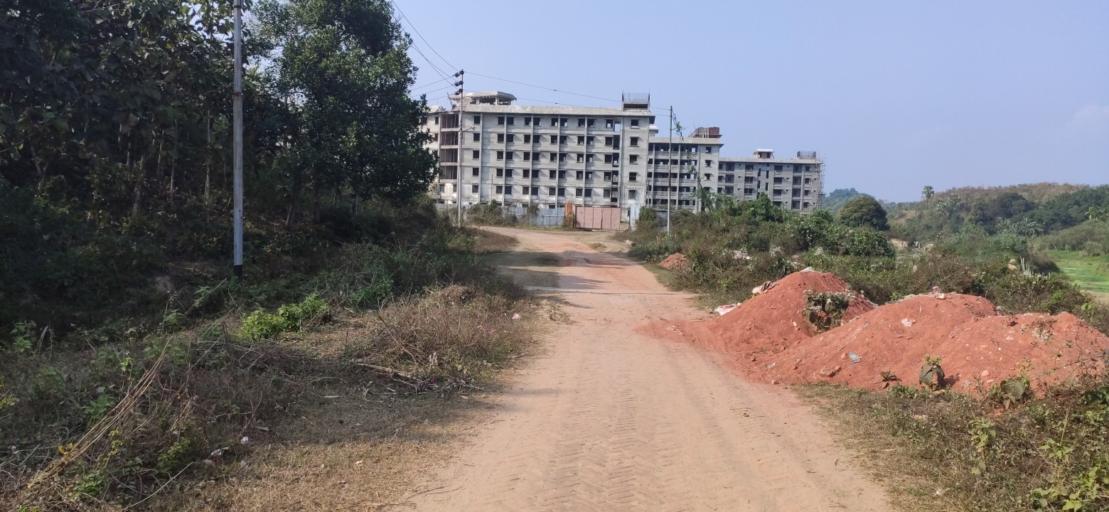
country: BD
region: Chittagong
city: Chittagong
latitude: 22.4757
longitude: 91.7844
